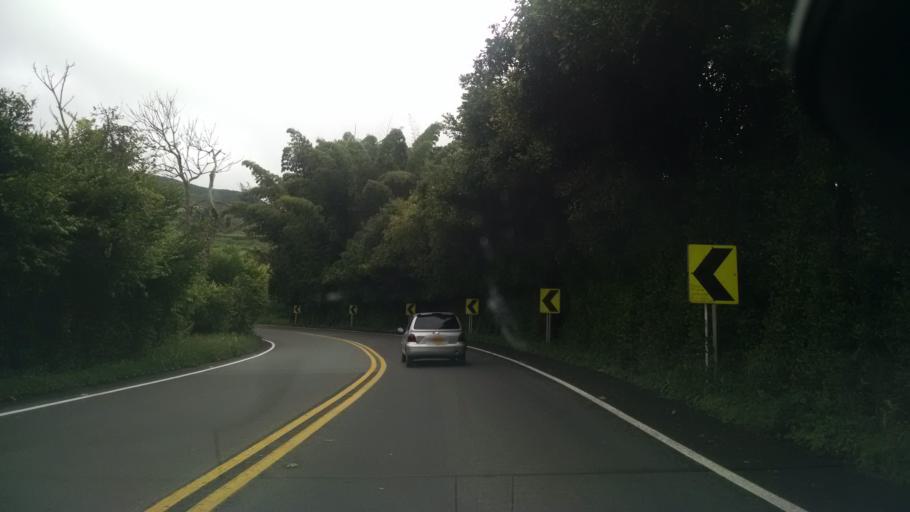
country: CO
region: Caldas
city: Palestina
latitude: 5.0256
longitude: -75.5971
